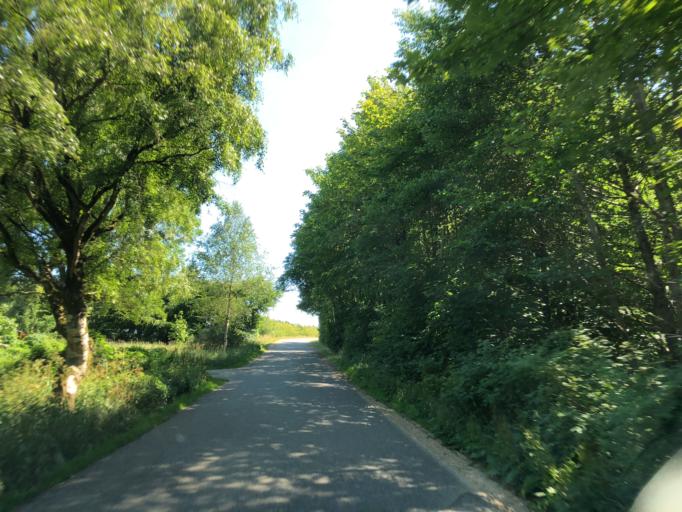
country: DK
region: Central Jutland
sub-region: Skive Kommune
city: Skive
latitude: 56.4601
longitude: 8.9761
